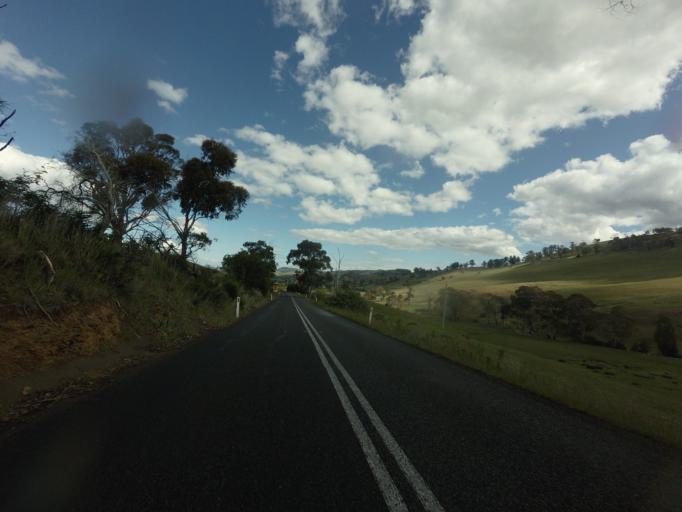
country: AU
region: Tasmania
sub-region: Brighton
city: Bridgewater
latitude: -42.5027
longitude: 147.3482
